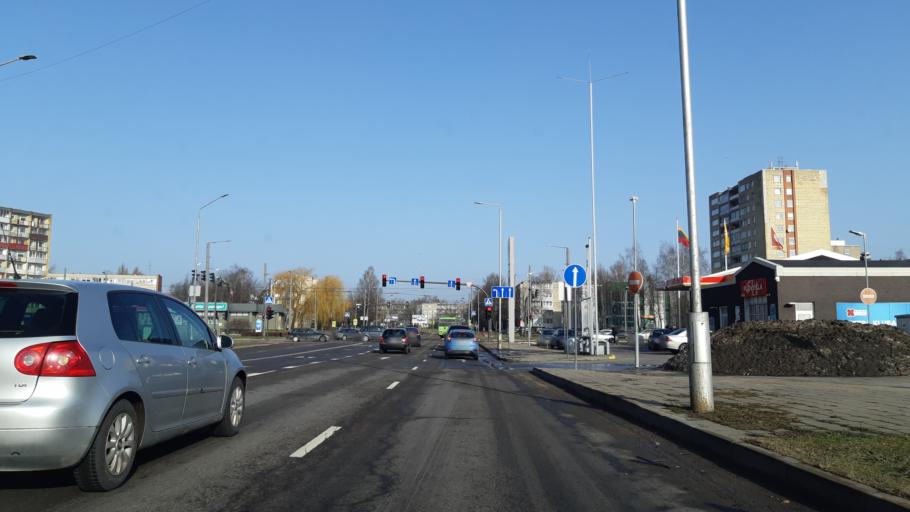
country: LT
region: Kauno apskritis
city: Dainava (Kaunas)
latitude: 54.9115
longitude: 23.9562
